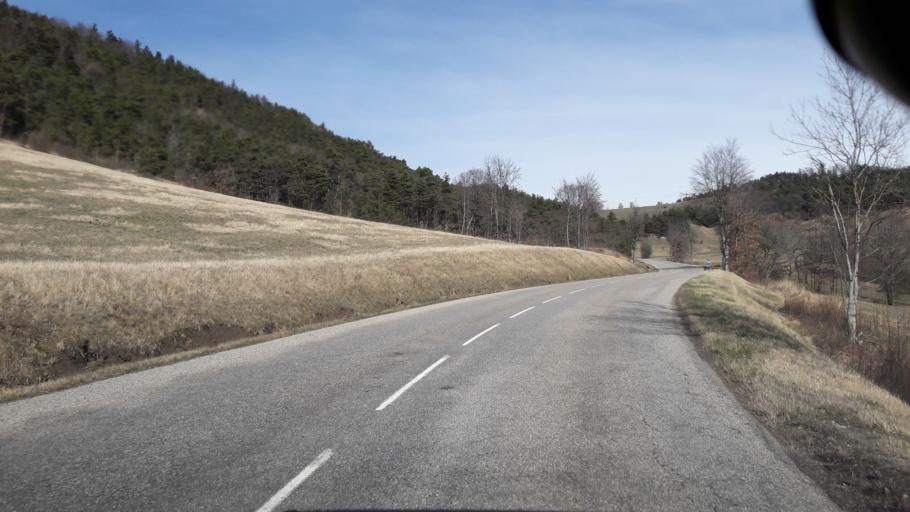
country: FR
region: Rhone-Alpes
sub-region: Departement de l'Isere
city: Mens
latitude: 44.8389
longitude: 5.7799
